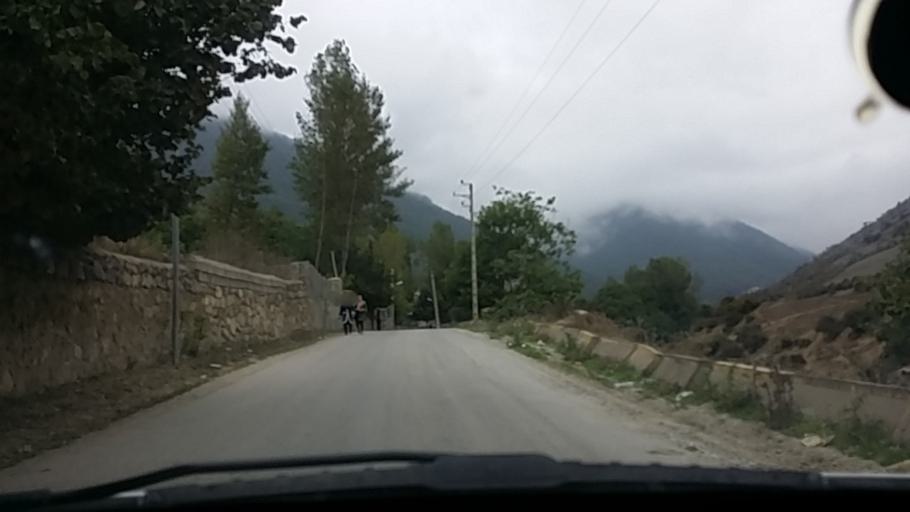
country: IR
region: Mazandaran
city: `Abbasabad
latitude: 36.4800
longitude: 51.1382
